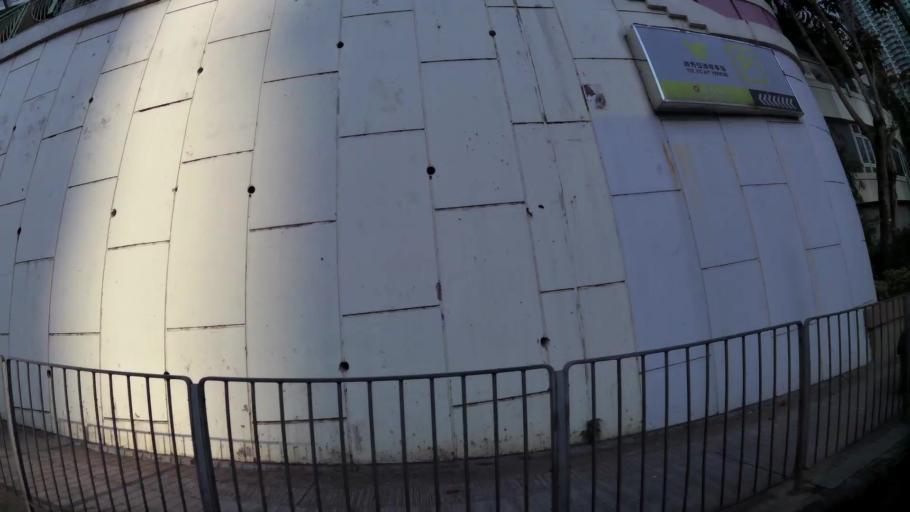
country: HK
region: Wanchai
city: Wan Chai
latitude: 22.2774
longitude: 114.1947
